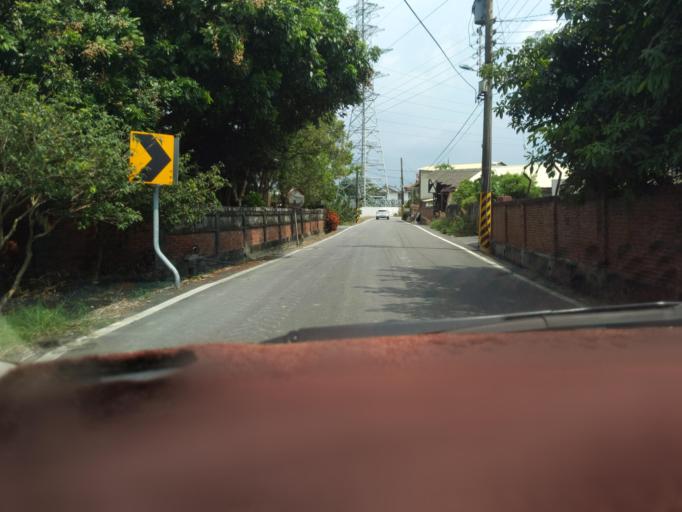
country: TW
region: Taiwan
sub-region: Yunlin
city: Douliu
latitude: 23.8555
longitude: 120.4876
